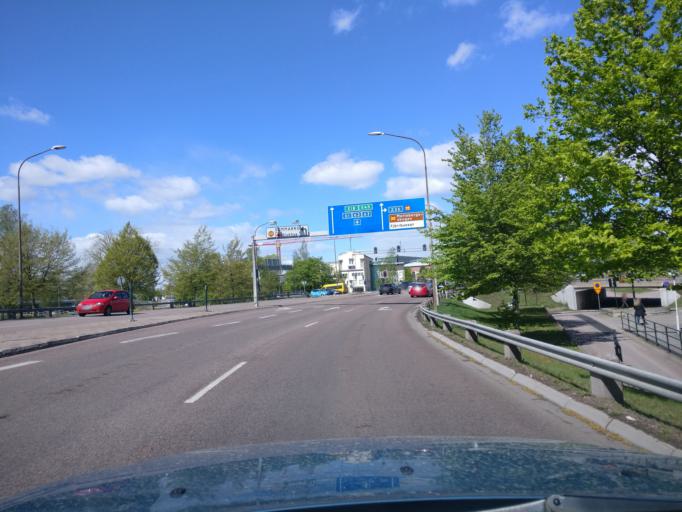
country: SE
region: Vaermland
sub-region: Karlstads Kommun
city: Karlstad
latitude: 59.3792
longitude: 13.4892
